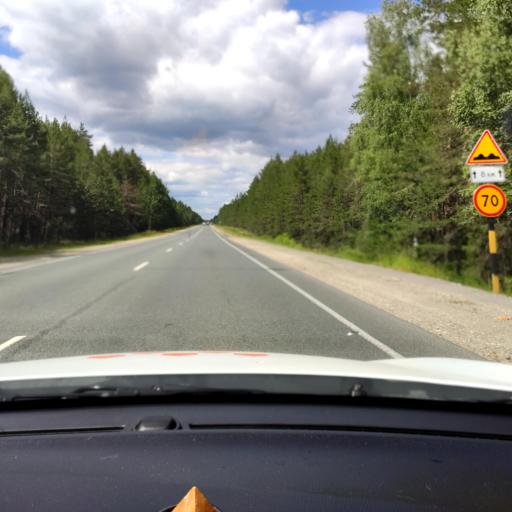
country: RU
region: Mariy-El
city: Krasnogorskiy
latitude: 56.0646
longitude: 48.3677
